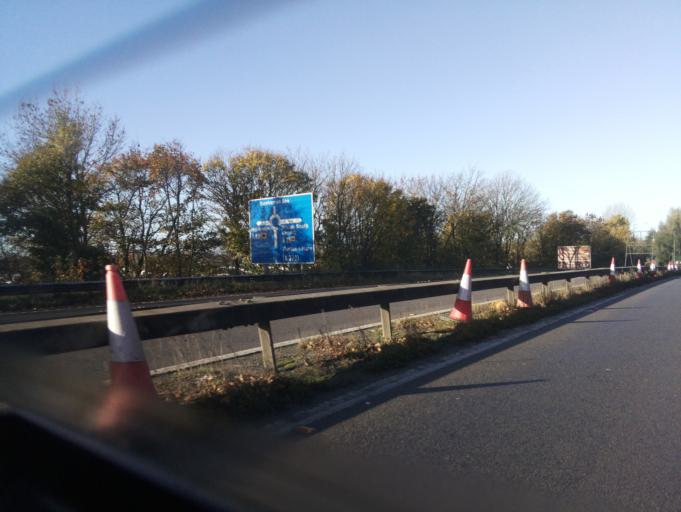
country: GB
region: England
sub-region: Somerset
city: Highbridge
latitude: 51.2366
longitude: -2.9492
